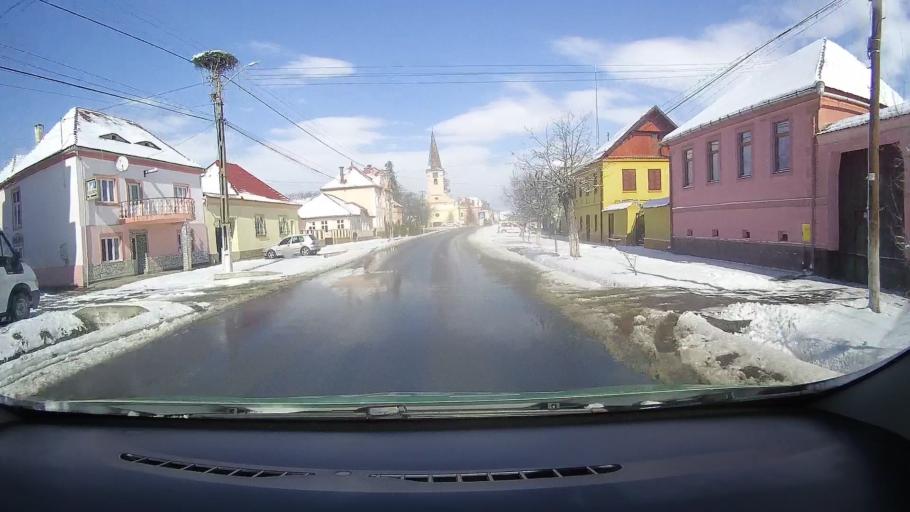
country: RO
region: Sibiu
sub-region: Comuna Nocrich
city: Nocrich
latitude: 45.8938
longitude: 24.4542
